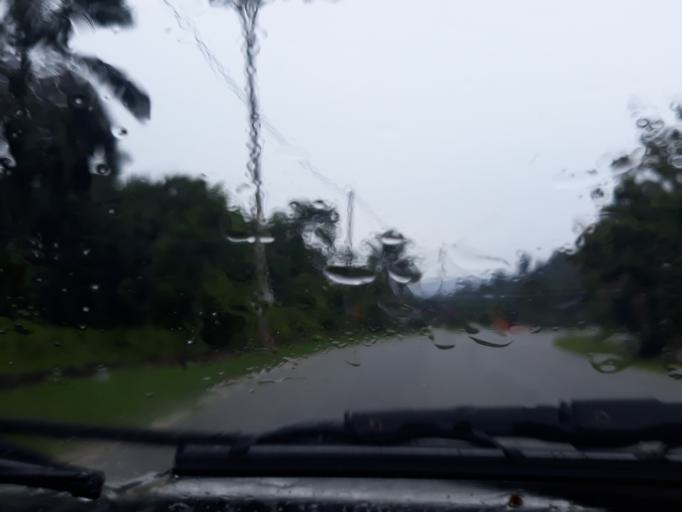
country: MY
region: Kedah
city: Kulim
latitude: 5.2742
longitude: 100.6158
